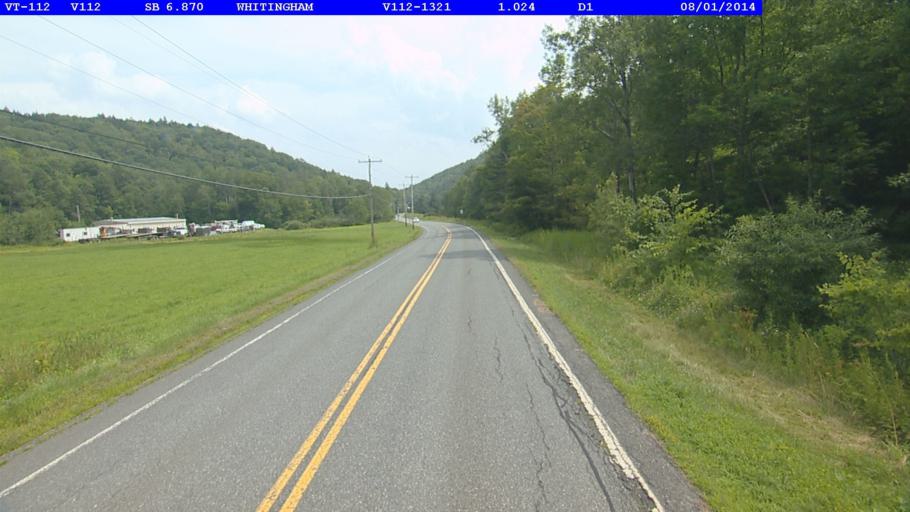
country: US
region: Vermont
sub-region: Windham County
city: Dover
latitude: 42.7891
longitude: -72.8186
